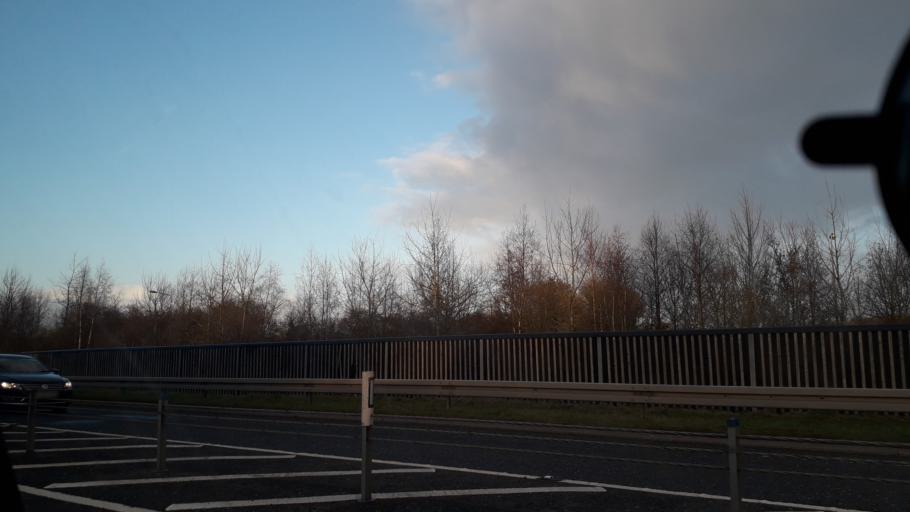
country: IE
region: Ulster
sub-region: County Monaghan
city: Monaghan
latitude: 54.2088
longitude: -6.8477
